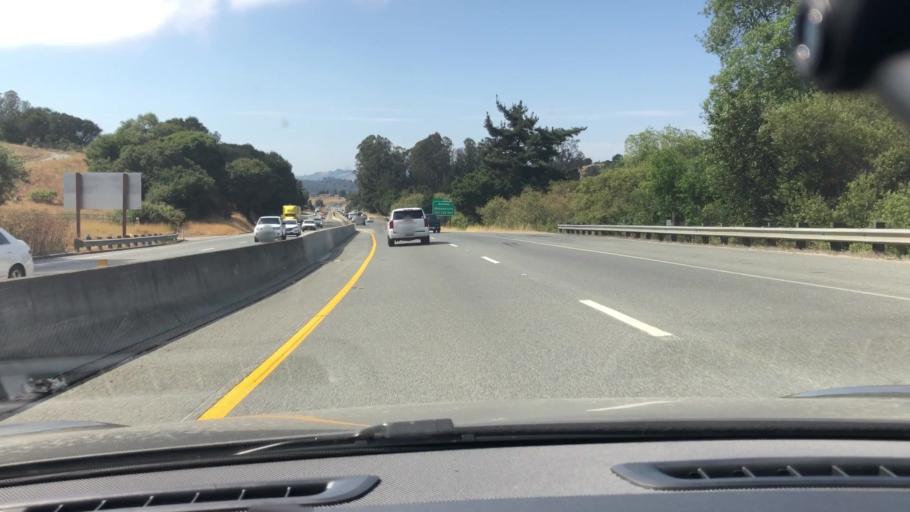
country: US
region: California
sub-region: San Benito County
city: Aromas
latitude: 36.8361
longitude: -121.6304
